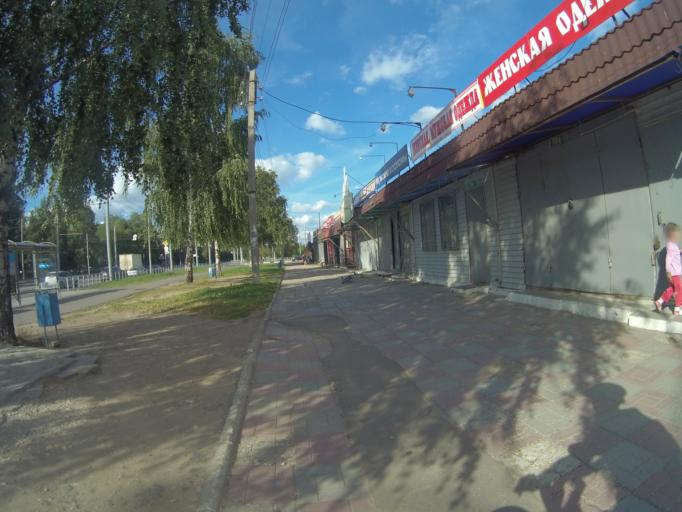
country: RU
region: Vladimir
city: Vladimir
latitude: 56.1409
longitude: 40.3666
